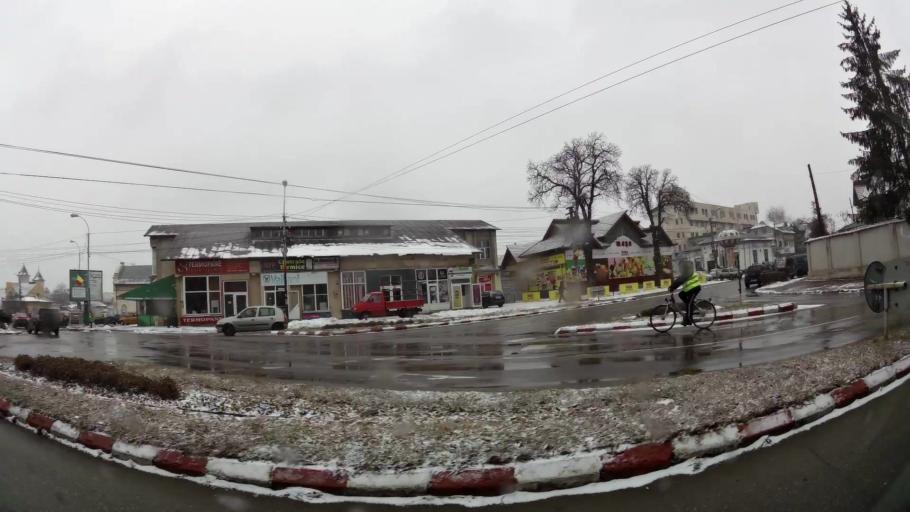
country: RO
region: Dambovita
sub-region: Municipiul Targoviste
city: Targoviste
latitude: 44.9335
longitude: 25.4552
